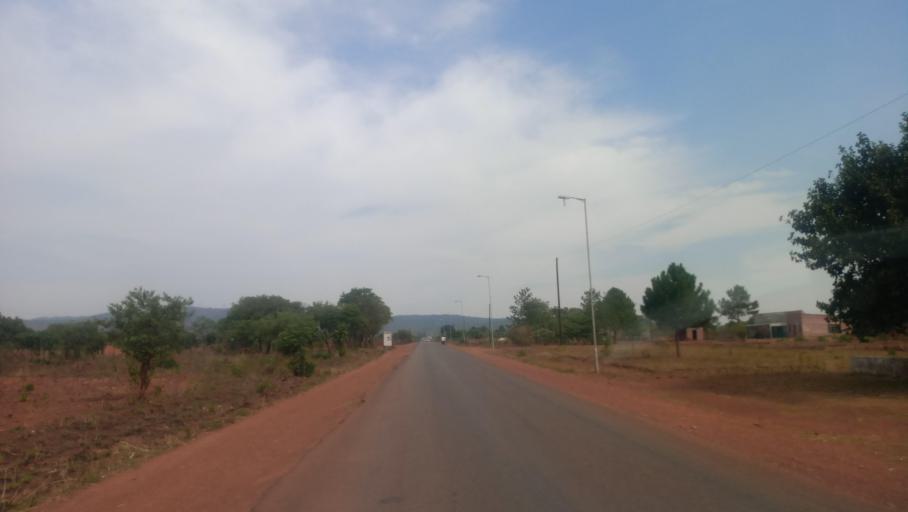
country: ZM
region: Northern
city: Mpika
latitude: -11.8368
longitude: 31.4305
